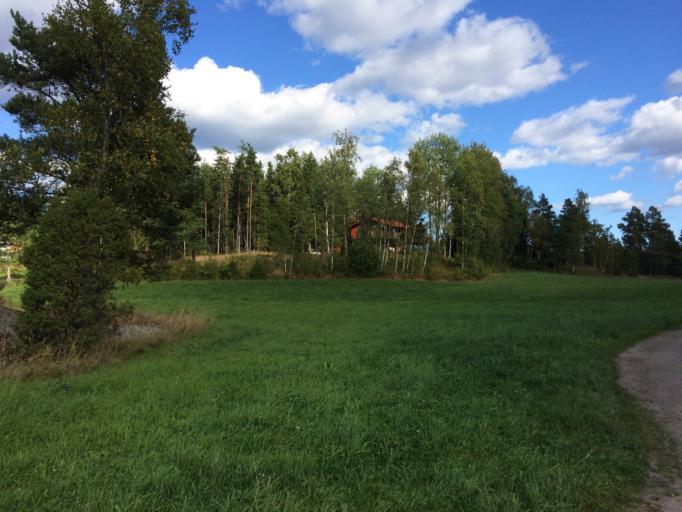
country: SE
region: Stockholm
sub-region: Norrtalje Kommun
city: Bjorko
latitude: 59.8473
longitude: 19.0253
